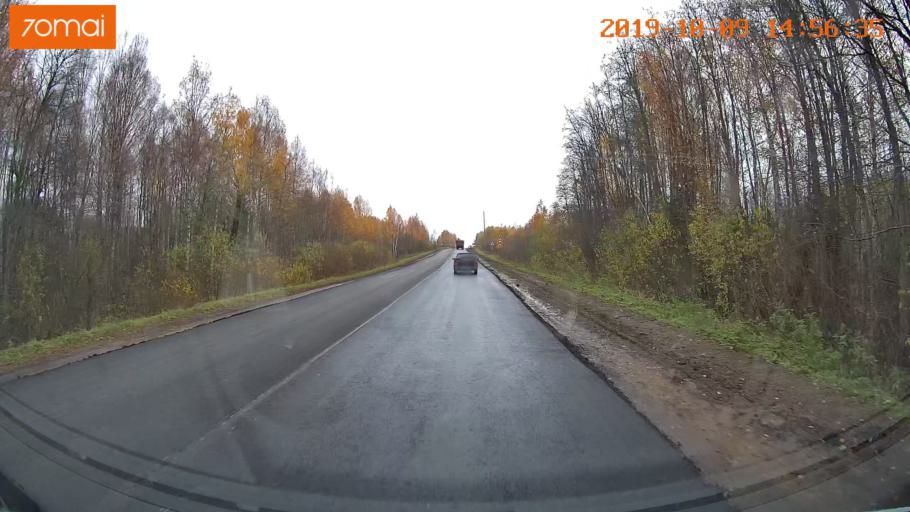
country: RU
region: Kostroma
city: Chistyye Bory
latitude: 58.3447
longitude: 41.6478
